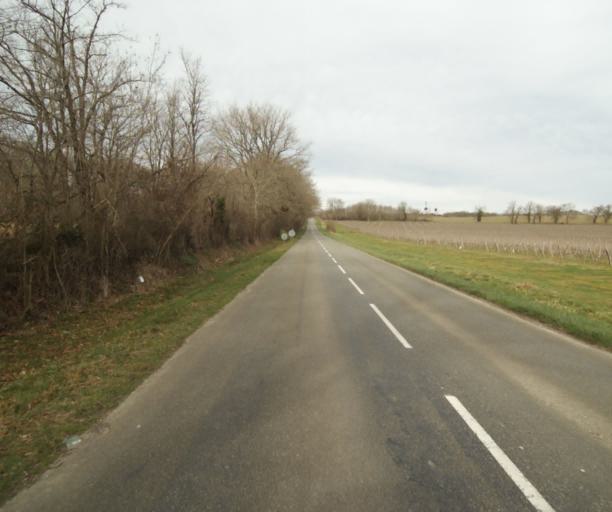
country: FR
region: Aquitaine
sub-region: Departement des Landes
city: Gabarret
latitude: 43.9553
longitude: 0.0085
